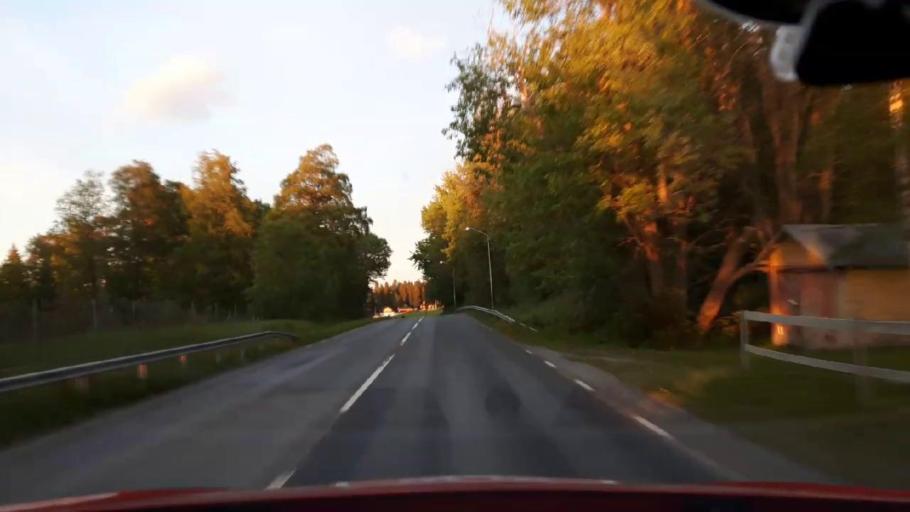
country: SE
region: Jaemtland
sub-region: OEstersunds Kommun
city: Ostersund
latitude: 63.1332
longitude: 14.6526
